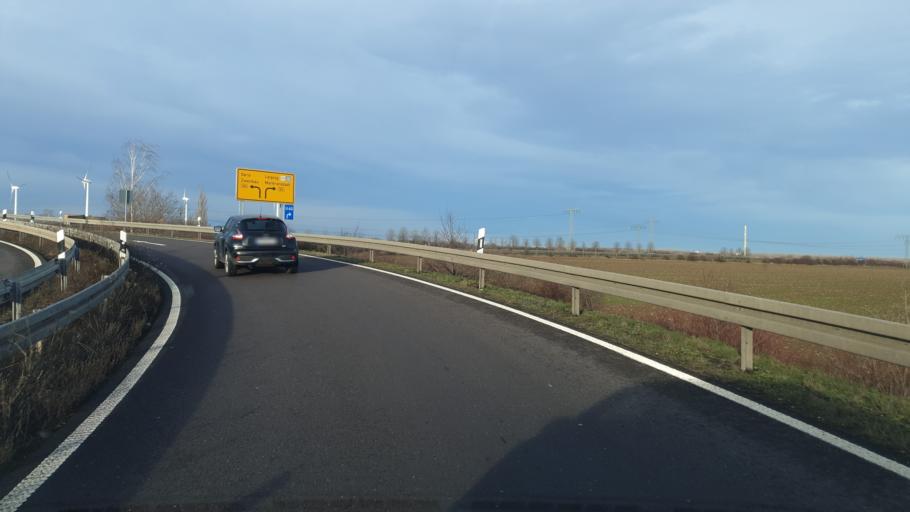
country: DE
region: Saxony
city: Markranstadt
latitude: 51.2640
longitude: 12.2711
